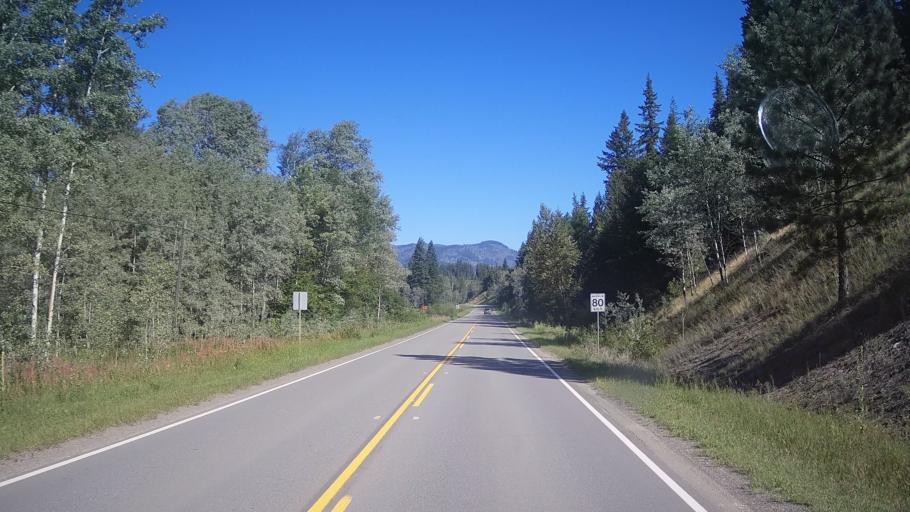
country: CA
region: British Columbia
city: Kamloops
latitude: 51.4366
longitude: -120.2084
